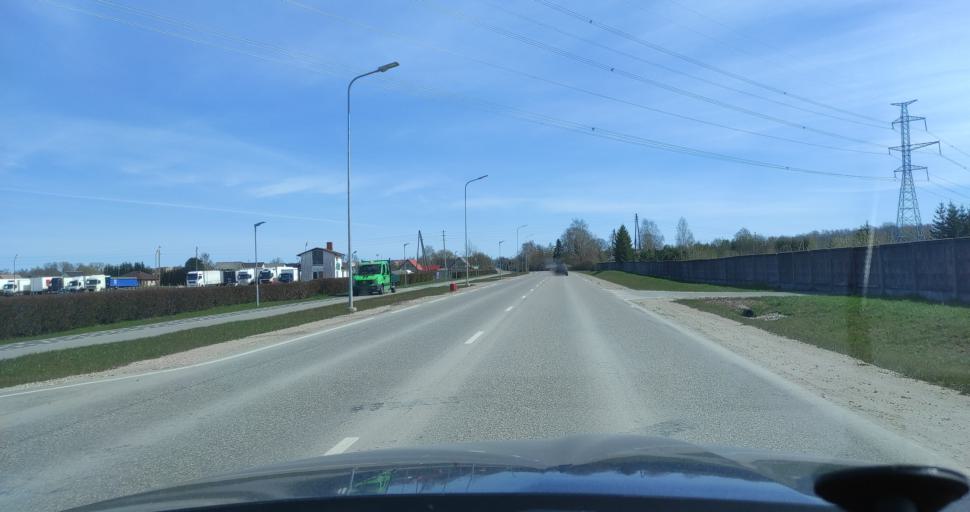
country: LV
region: Talsu Rajons
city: Talsi
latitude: 57.2354
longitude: 22.5669
